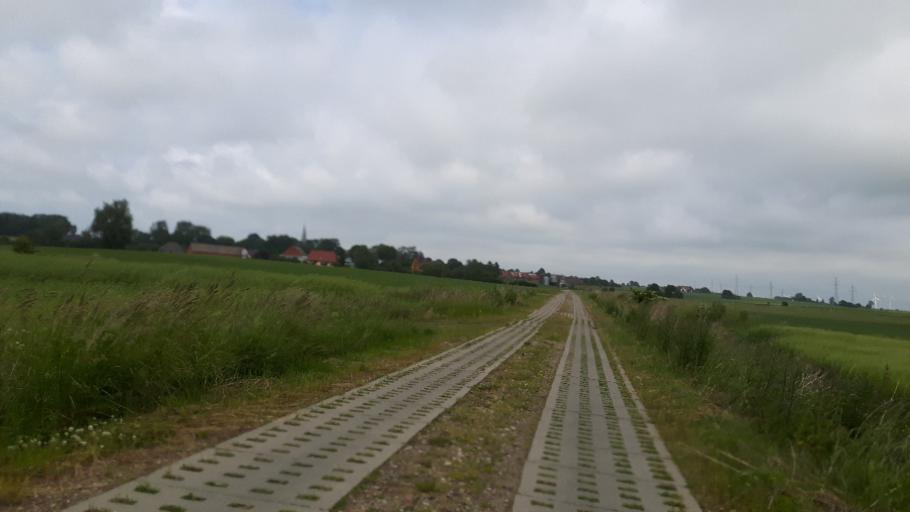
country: PL
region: West Pomeranian Voivodeship
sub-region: Powiat koszalinski
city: Sianow
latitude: 54.2905
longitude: 16.2688
